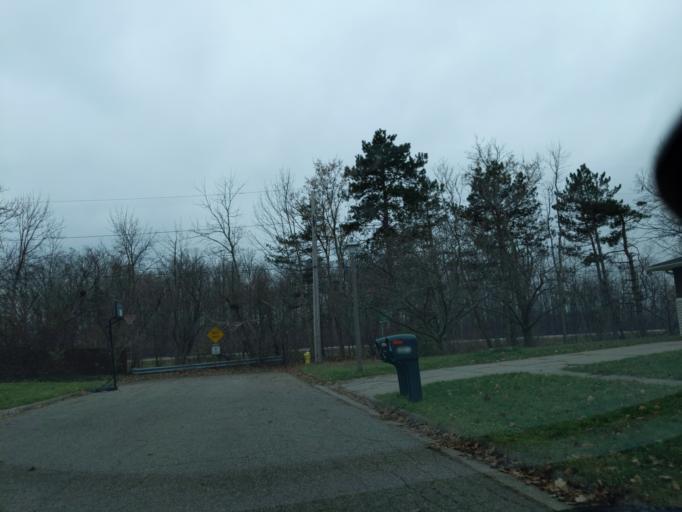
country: US
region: Michigan
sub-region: Eaton County
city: Waverly
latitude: 42.7205
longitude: -84.6282
